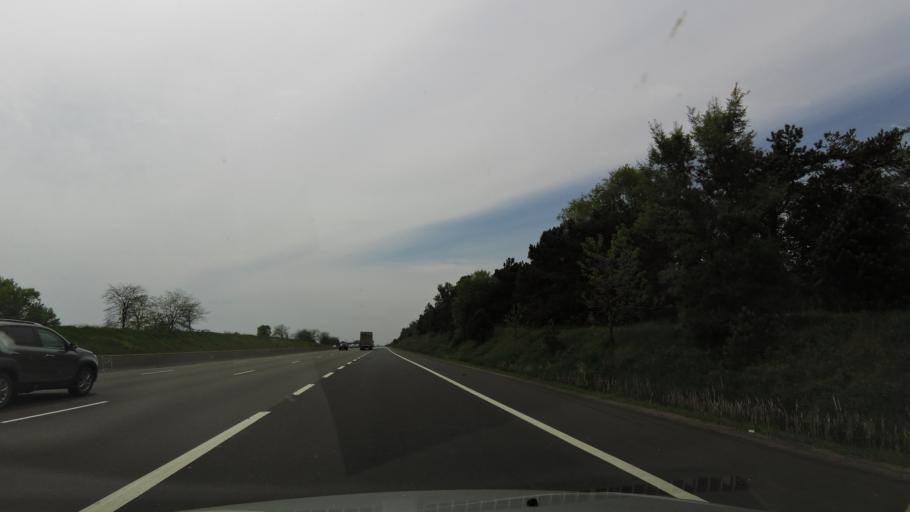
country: CA
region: Ontario
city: Oshawa
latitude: 43.9099
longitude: -78.5900
